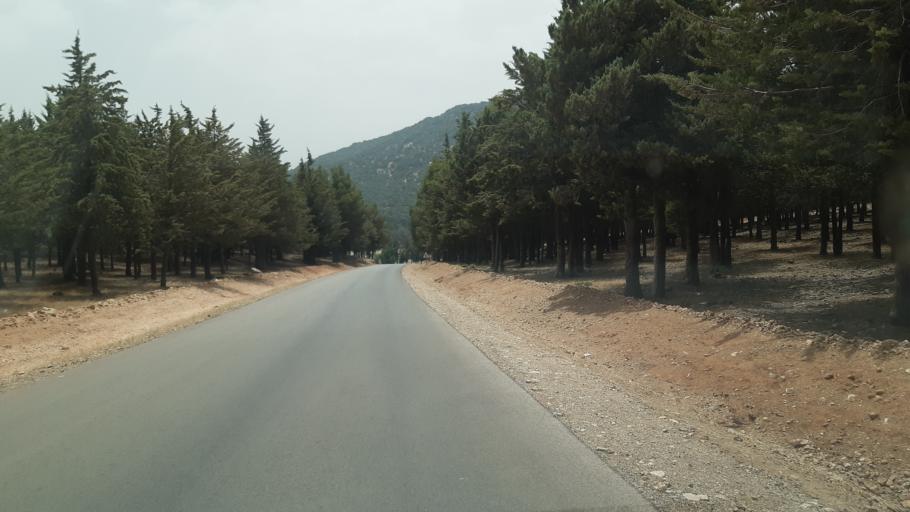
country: MA
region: Meknes-Tafilalet
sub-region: Ifrane
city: Ifrane
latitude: 33.6603
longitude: -5.0429
